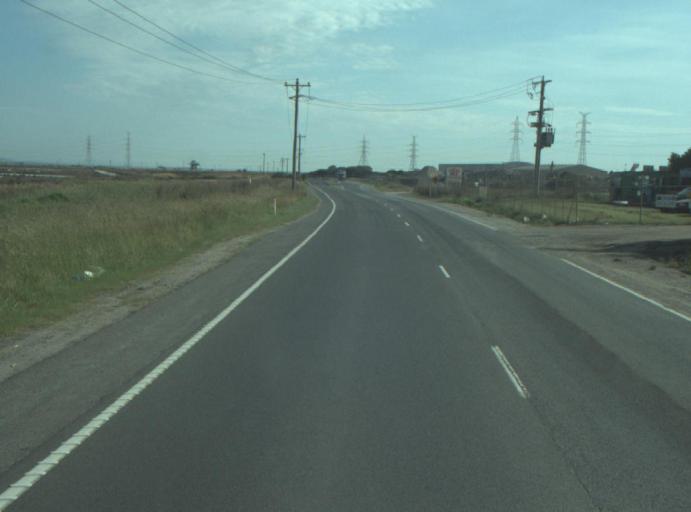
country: AU
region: Victoria
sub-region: Greater Geelong
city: Leopold
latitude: -38.1606
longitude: 144.4298
